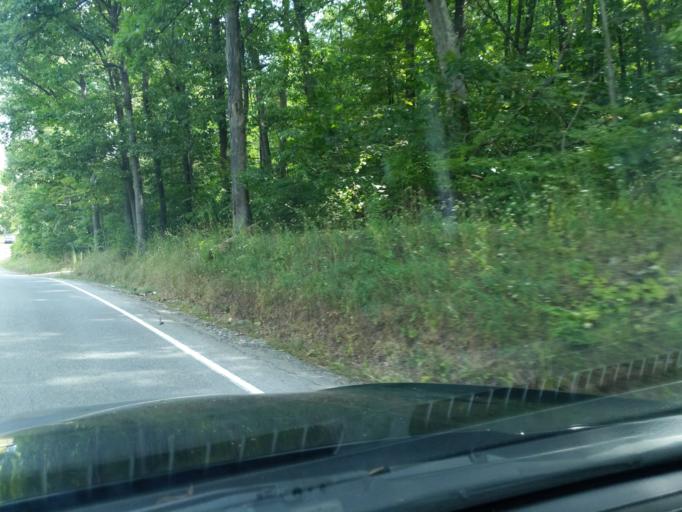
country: US
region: Pennsylvania
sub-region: Blair County
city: Hollidaysburg
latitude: 40.3963
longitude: -78.3973
